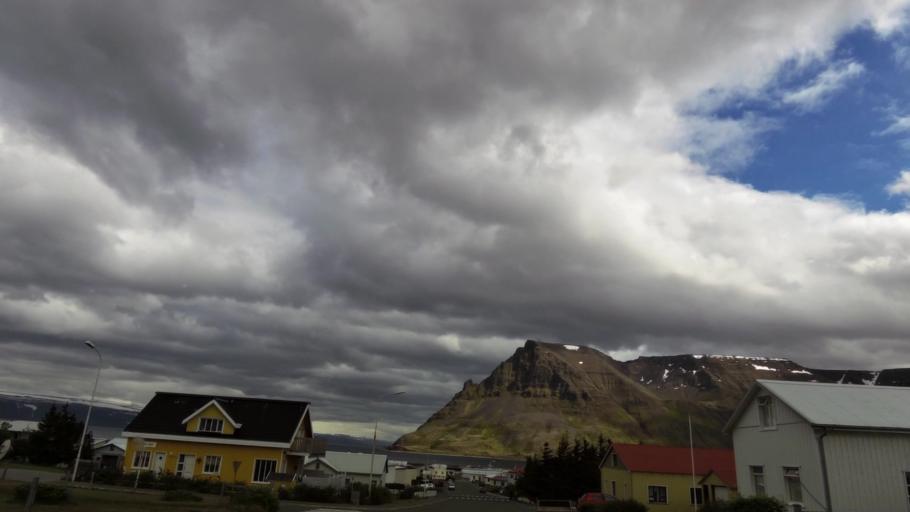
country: IS
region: Westfjords
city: Isafjoerdur
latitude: 66.1580
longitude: -23.2582
